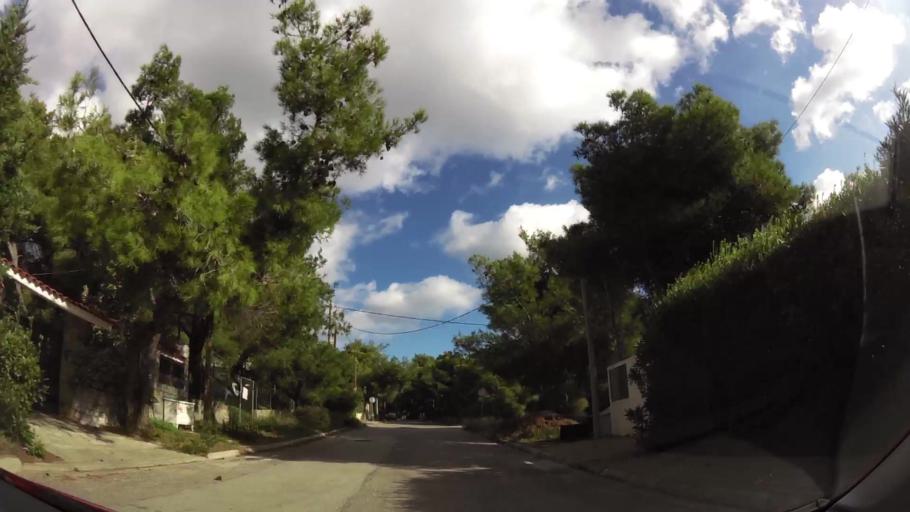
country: GR
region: Attica
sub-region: Nomarchia Anatolikis Attikis
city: Thrakomakedones
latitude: 38.1276
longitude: 23.7620
